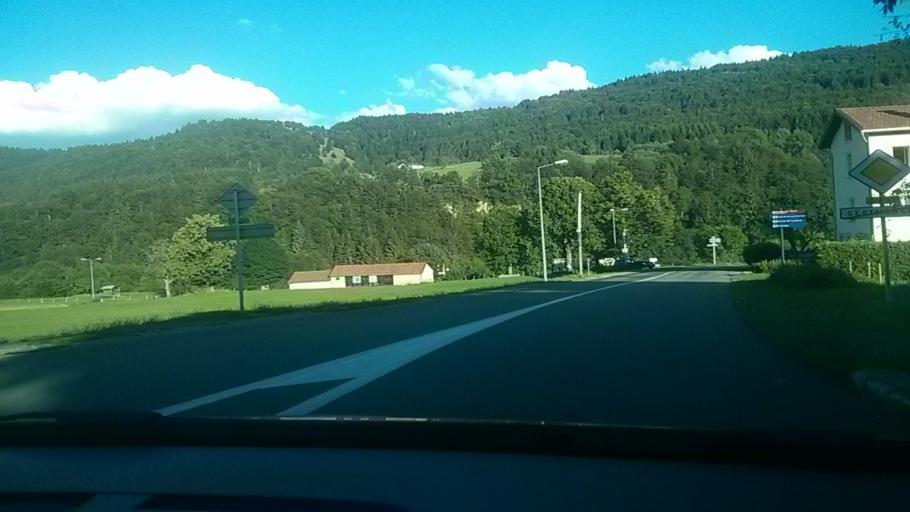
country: FR
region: Franche-Comte
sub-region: Departement du Jura
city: Saint-Claude
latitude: 46.3691
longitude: 5.9140
